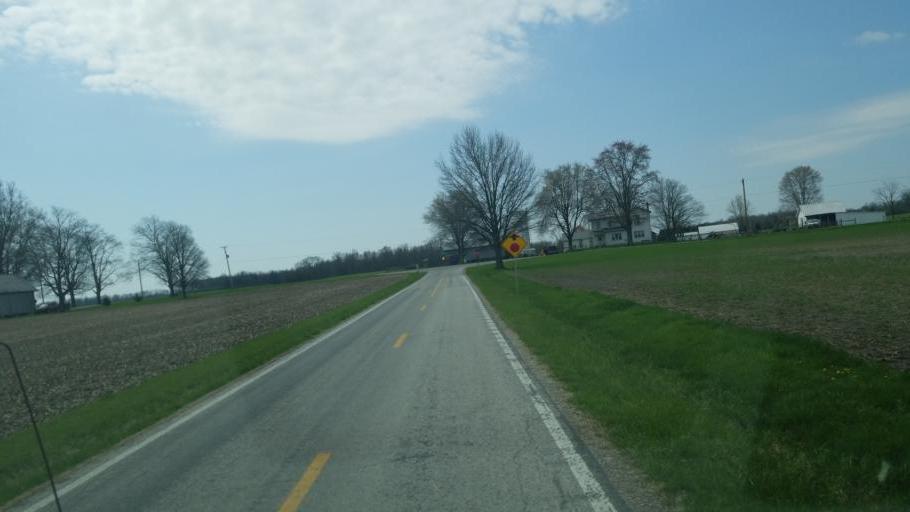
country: US
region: Ohio
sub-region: Delaware County
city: Ashley
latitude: 40.3633
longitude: -83.0159
